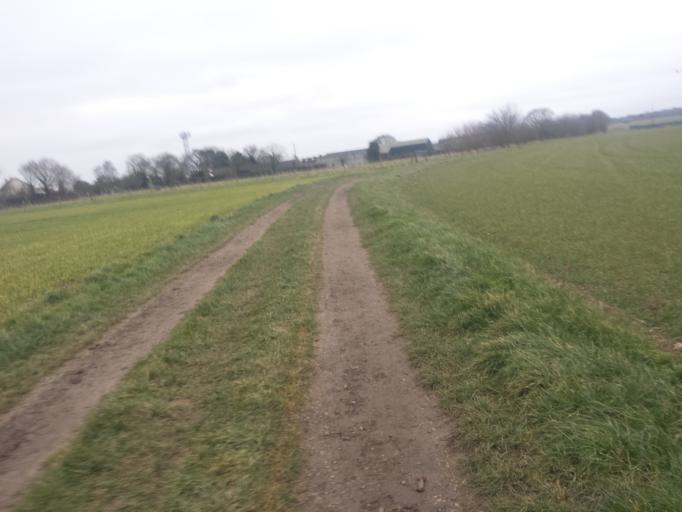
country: GB
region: England
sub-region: Essex
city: Little Clacton
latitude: 51.8543
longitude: 1.1598
